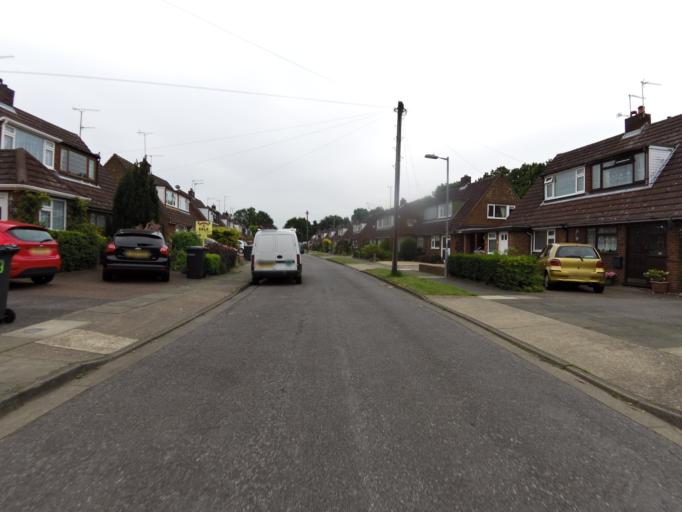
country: GB
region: England
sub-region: Suffolk
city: Kesgrave
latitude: 52.0478
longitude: 1.1967
